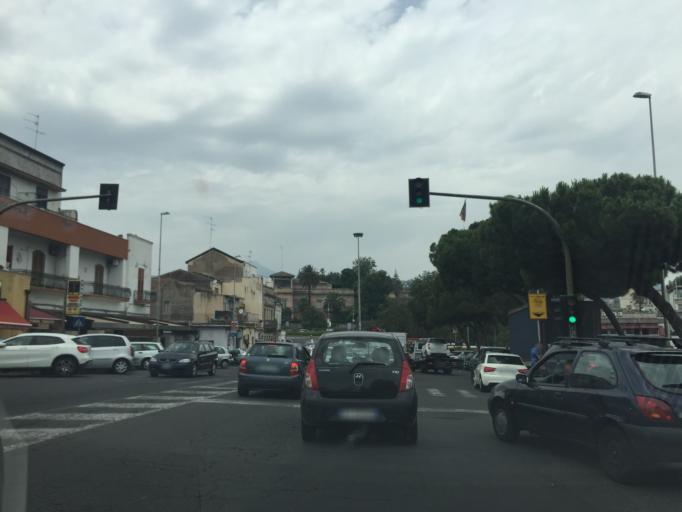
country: IT
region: Sicily
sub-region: Catania
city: Cerza
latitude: 37.5303
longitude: 15.1121
